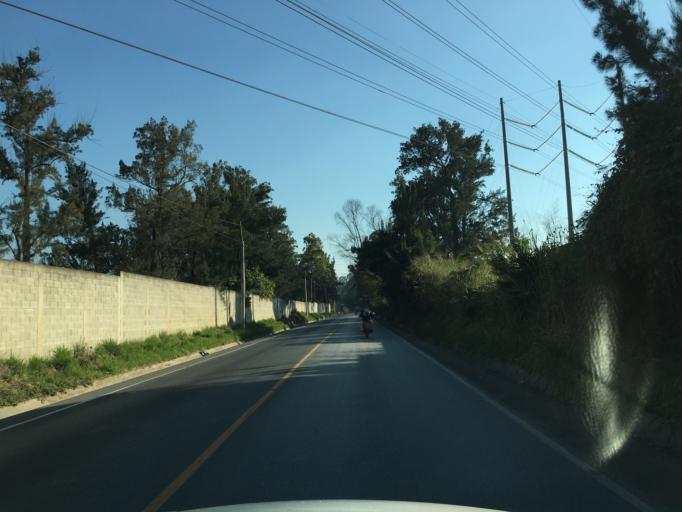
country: GT
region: Guatemala
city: Villa Nueva
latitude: 14.5262
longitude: -90.6168
